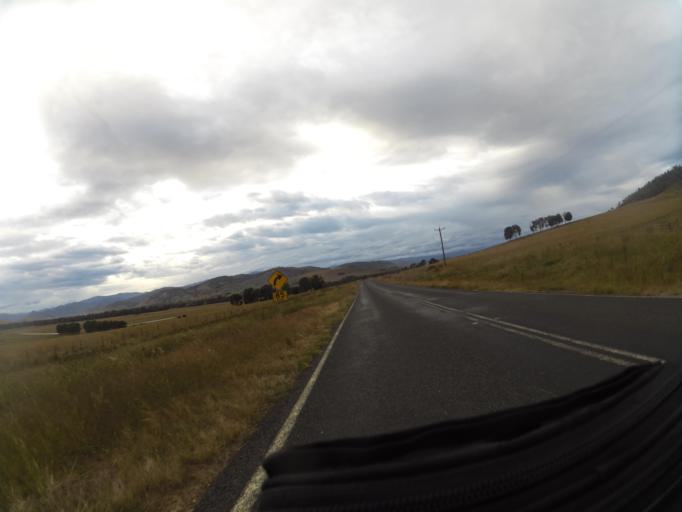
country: AU
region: New South Wales
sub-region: Snowy River
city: Jindabyne
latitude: -36.0747
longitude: 147.9696
